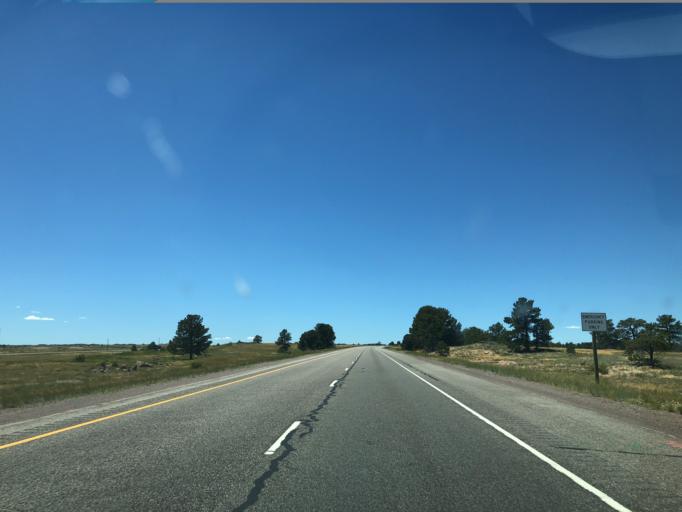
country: US
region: Wyoming
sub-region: Albany County
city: Laramie
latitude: 41.1263
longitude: -105.3204
